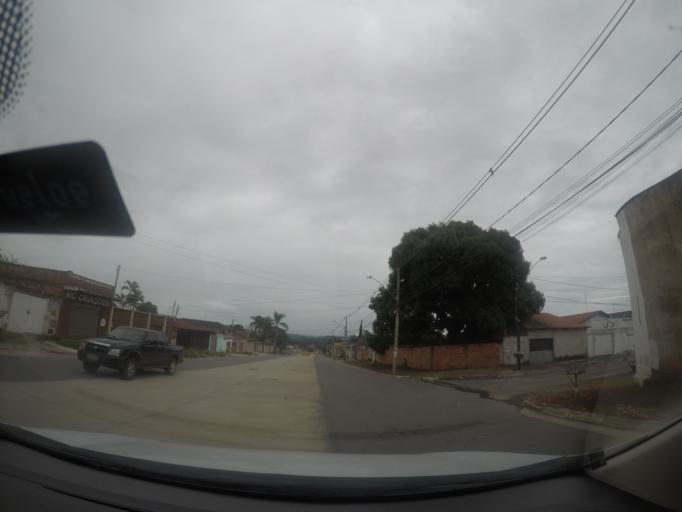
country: BR
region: Goias
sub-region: Goiania
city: Goiania
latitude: -16.6183
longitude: -49.3001
